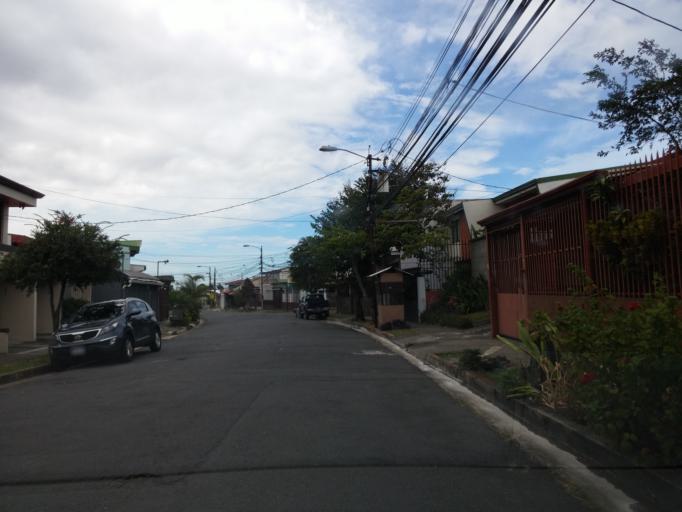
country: CR
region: San Jose
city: San Jose
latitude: 9.9297
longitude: -84.1075
